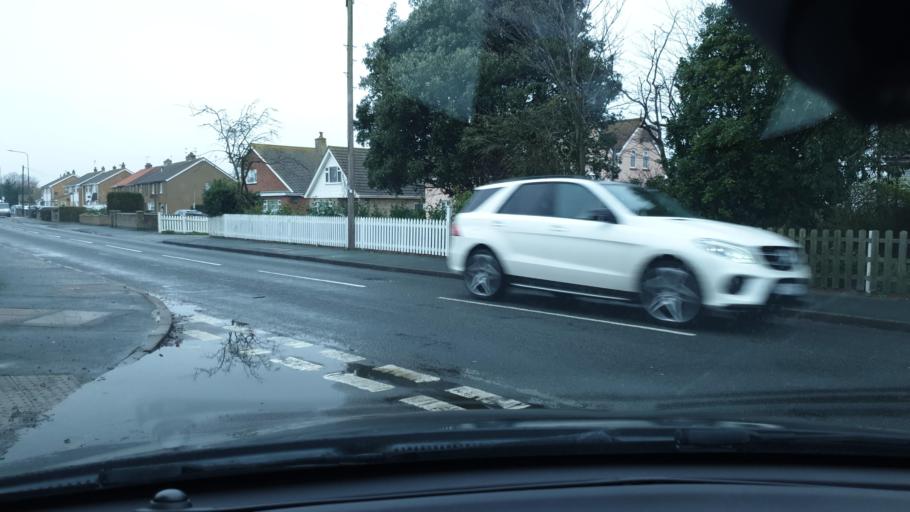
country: GB
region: England
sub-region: Essex
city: Clacton-on-Sea
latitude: 51.8049
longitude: 1.2002
